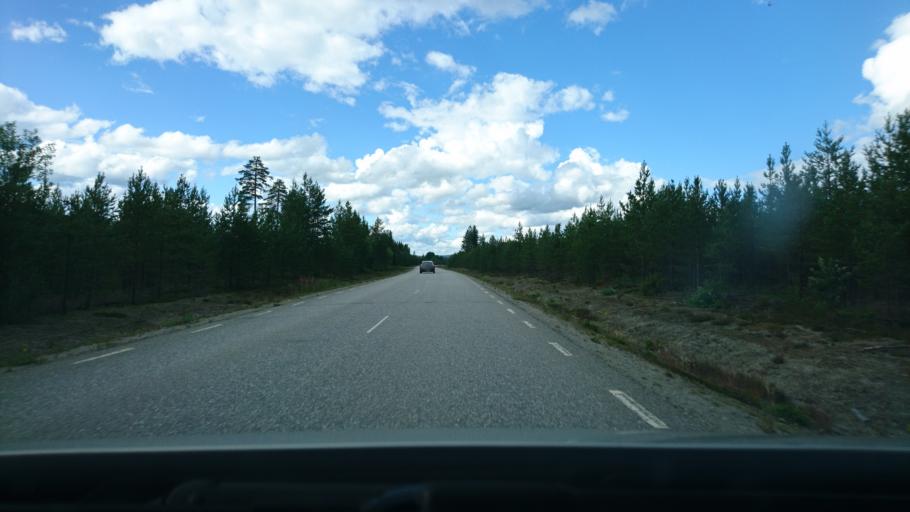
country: SE
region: Vaesterbotten
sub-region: Asele Kommun
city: Asele
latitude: 63.9590
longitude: 17.2697
